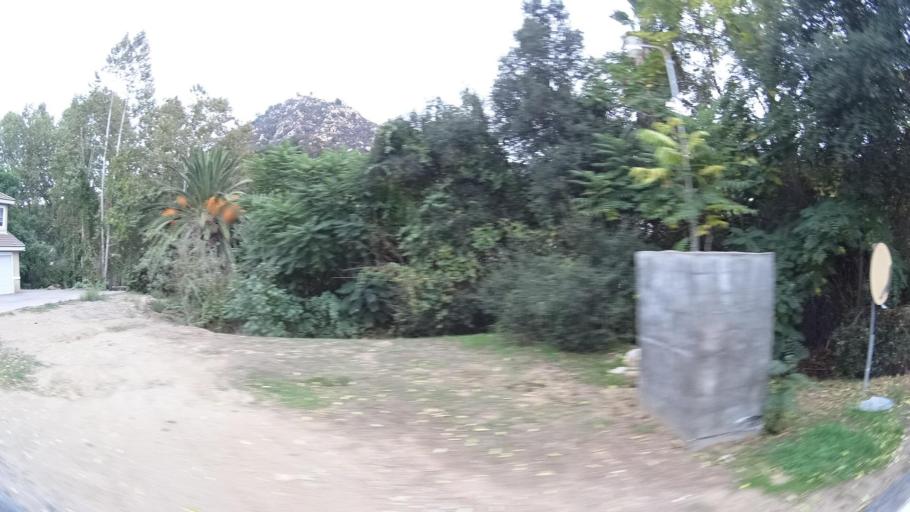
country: US
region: California
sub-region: San Diego County
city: Harbison Canyon
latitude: 32.8157
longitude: -116.8345
